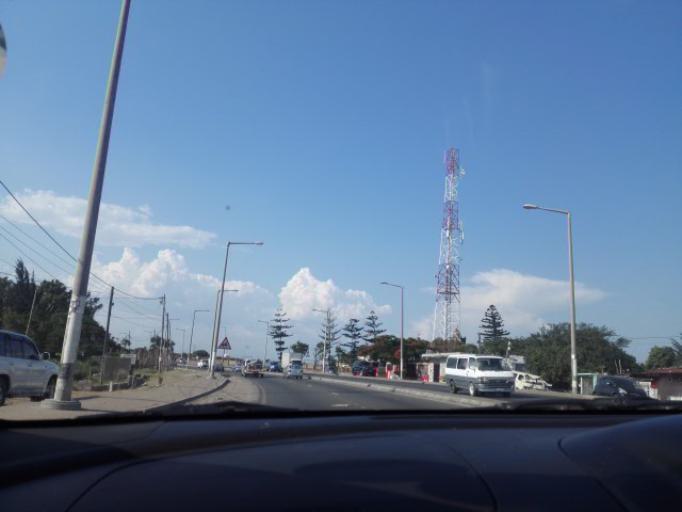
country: MZ
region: Maputo City
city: Maputo
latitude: -25.8815
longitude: 32.5680
